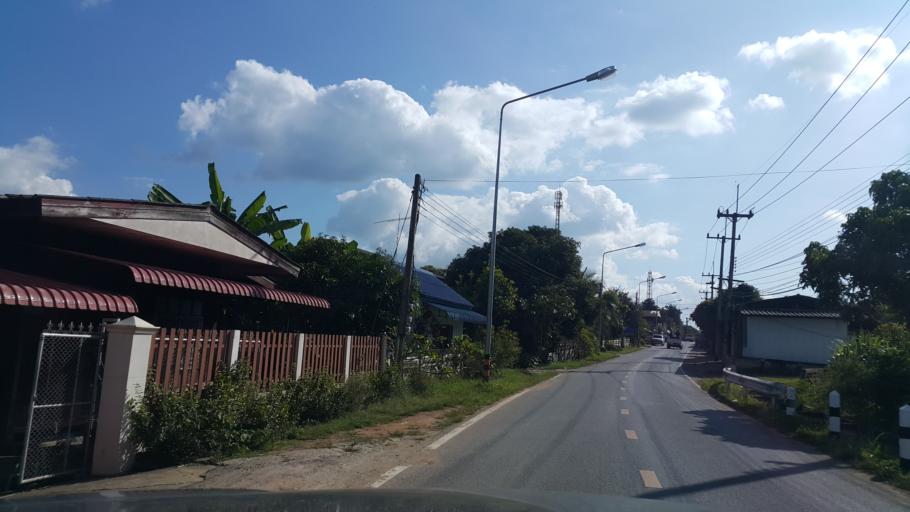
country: TH
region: Lamphun
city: Mae Tha
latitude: 18.5509
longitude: 99.2461
